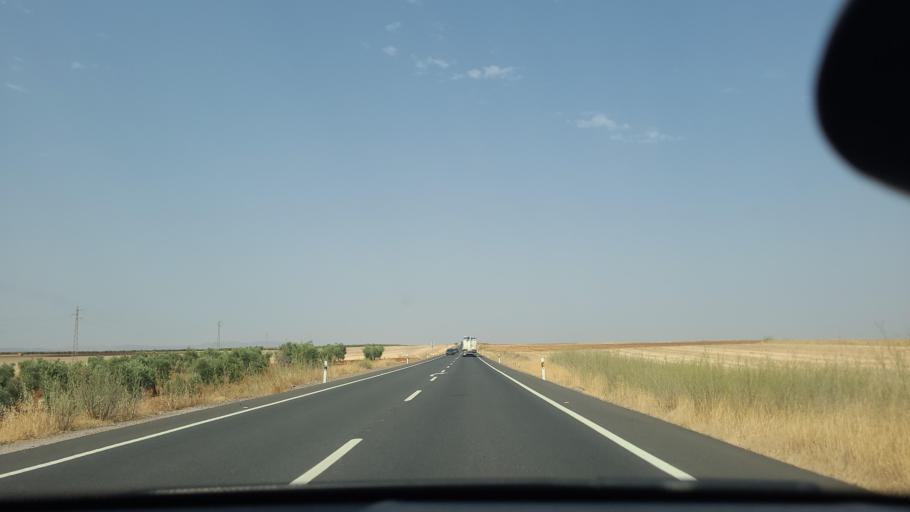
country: ES
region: Extremadura
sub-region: Provincia de Badajoz
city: Berlanga
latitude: 38.2664
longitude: -5.7690
